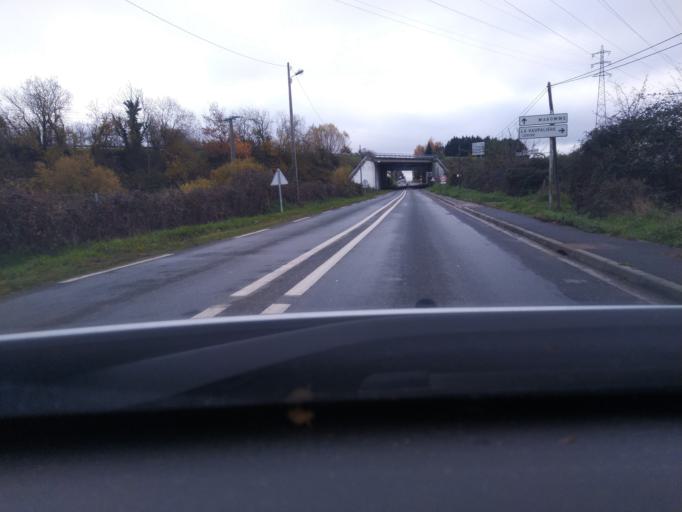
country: FR
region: Haute-Normandie
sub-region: Departement de la Seine-Maritime
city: La Vaupaliere
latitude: 49.4917
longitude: 0.9975
